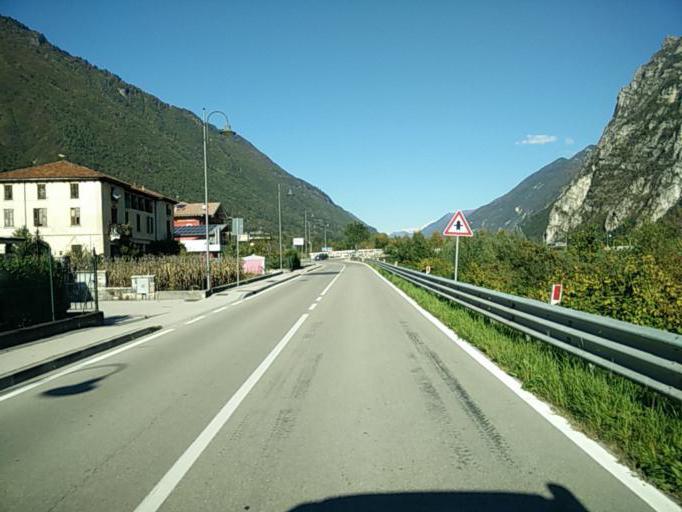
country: IT
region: Trentino-Alto Adige
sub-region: Provincia di Trento
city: Storo
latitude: 45.8532
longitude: 10.5667
